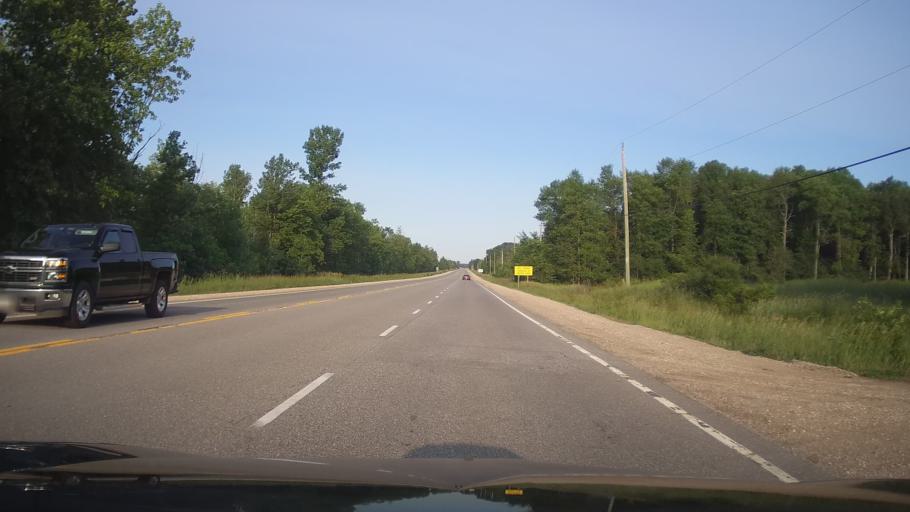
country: CA
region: Ontario
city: Perth
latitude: 44.8781
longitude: -76.3420
